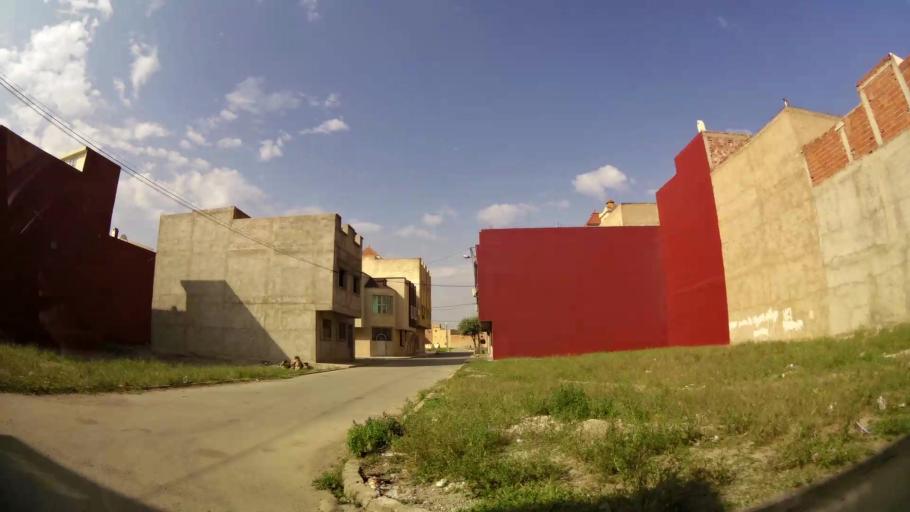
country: MA
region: Oriental
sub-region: Oujda-Angad
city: Oujda
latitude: 34.6887
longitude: -1.8994
